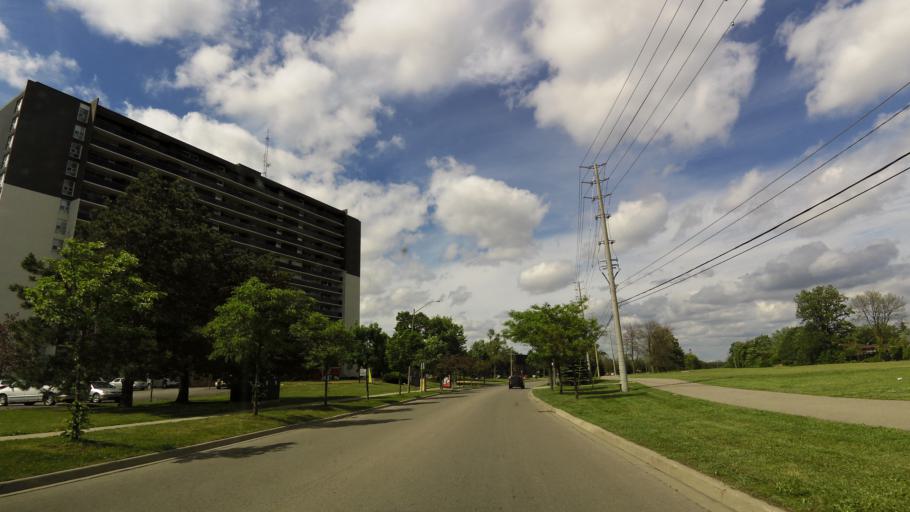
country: CA
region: Ontario
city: Mississauga
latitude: 43.5266
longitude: -79.6608
